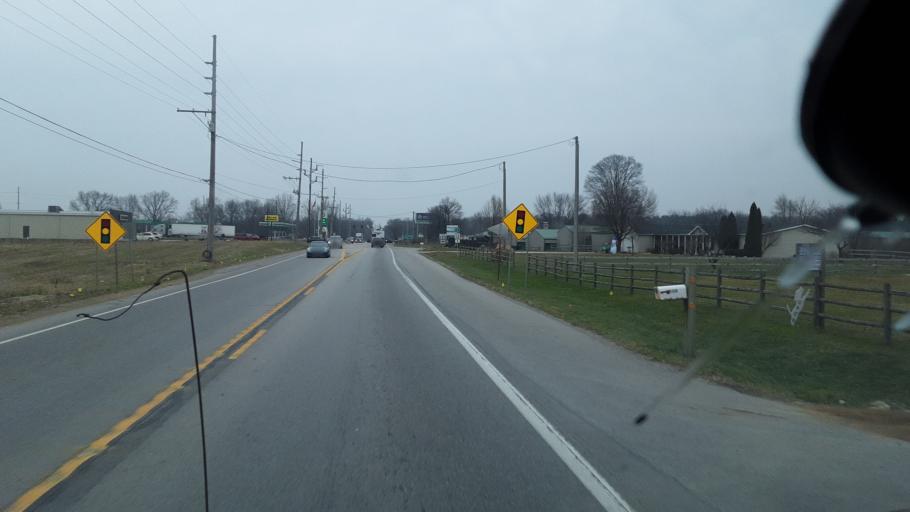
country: US
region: Indiana
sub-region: Elkhart County
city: Middlebury
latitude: 41.7230
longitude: -85.6844
